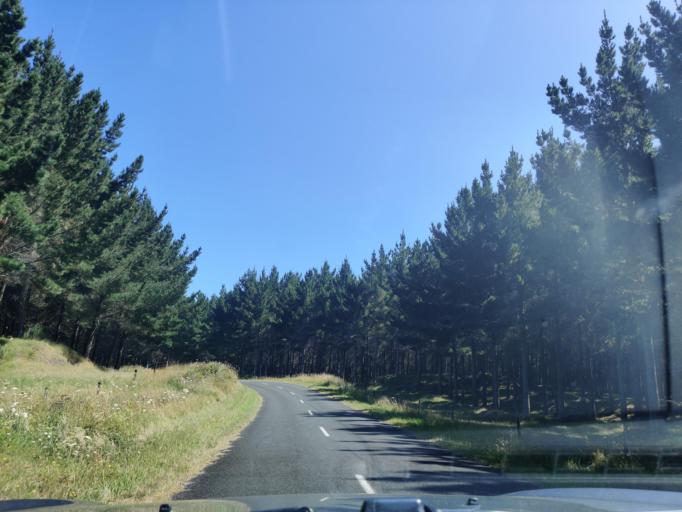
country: NZ
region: Waikato
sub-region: Waikato District
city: Raglan
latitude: -38.0675
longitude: 174.7907
